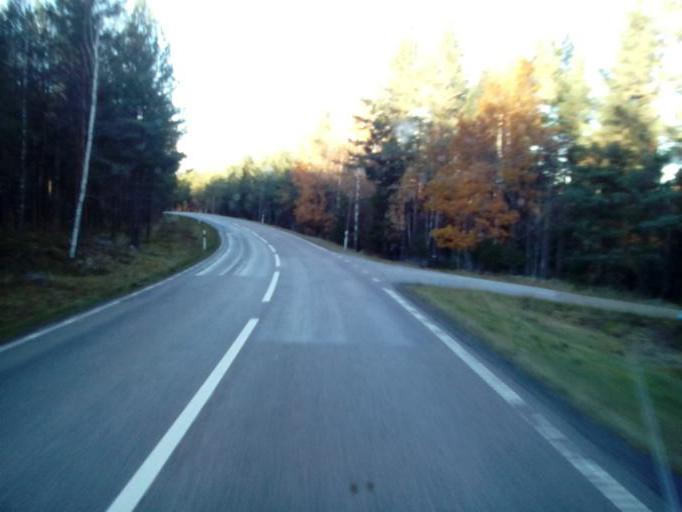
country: SE
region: OErebro
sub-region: Hallsbergs Kommun
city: Palsboda
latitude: 58.8211
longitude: 15.4139
